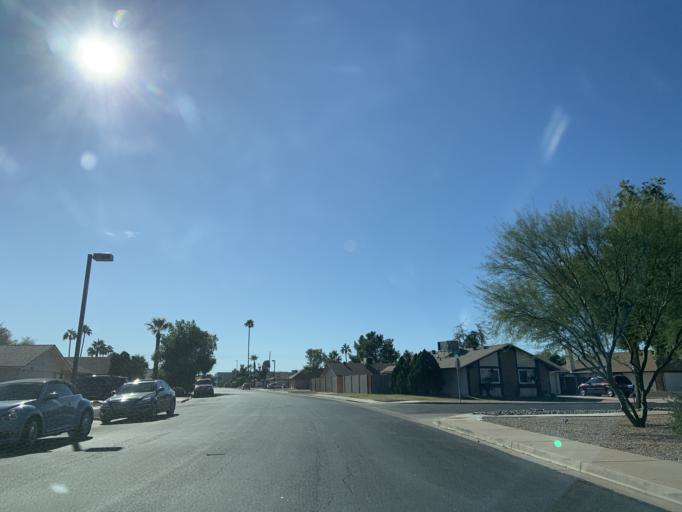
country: US
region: Arizona
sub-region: Maricopa County
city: San Carlos
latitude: 33.3670
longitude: -111.8678
